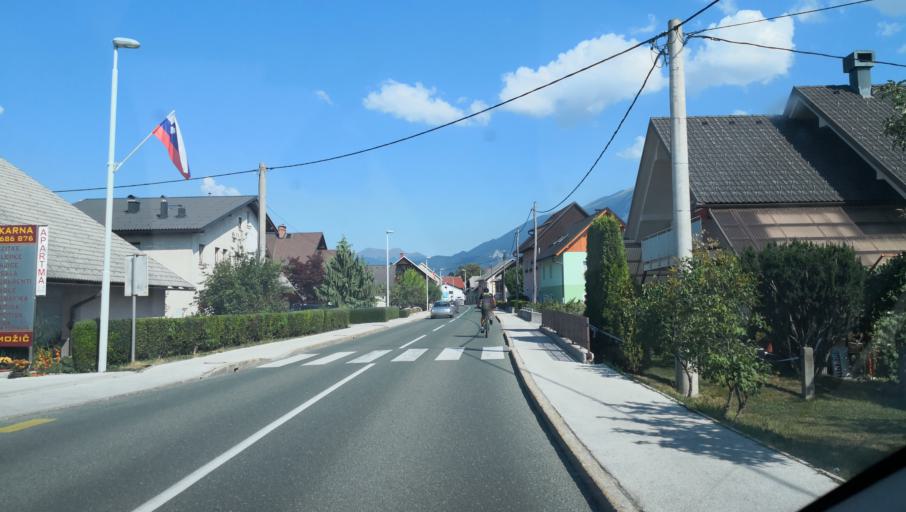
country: SI
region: Radovljica
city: Lesce
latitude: 46.3581
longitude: 14.1627
